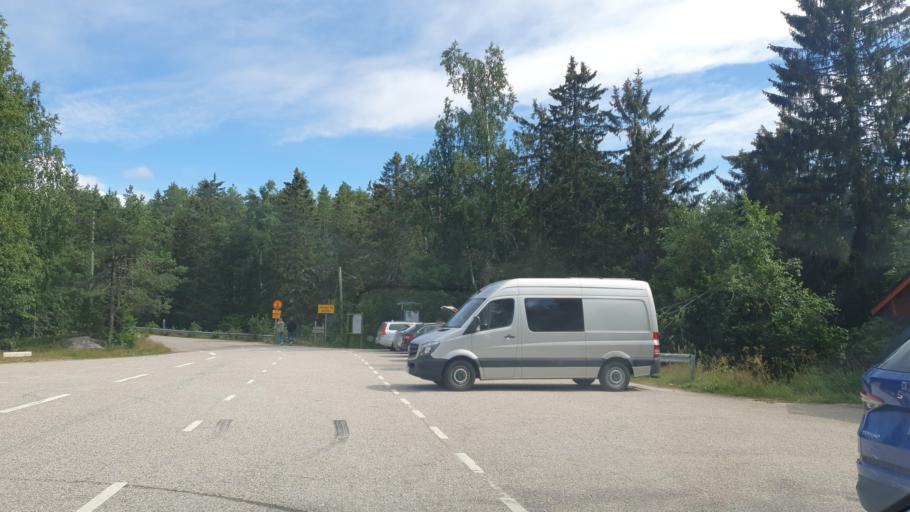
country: FI
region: Kainuu
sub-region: Kajaani
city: Vuokatti
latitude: 64.1282
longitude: 28.2646
